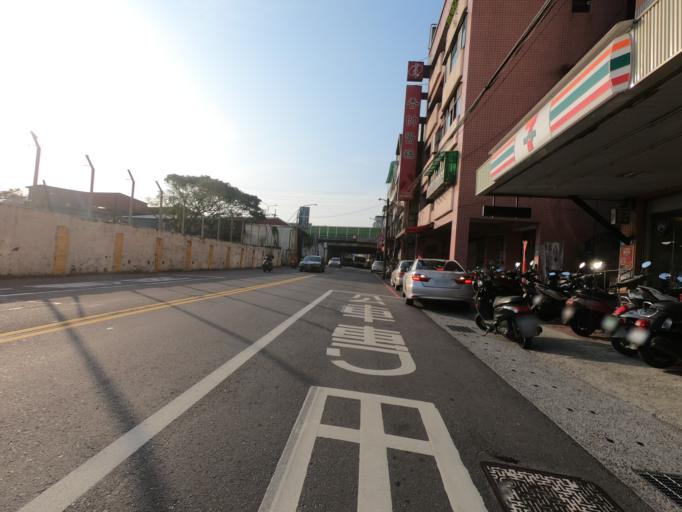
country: TW
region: Taiwan
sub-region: Keelung
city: Keelung
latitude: 25.0728
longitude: 121.6518
